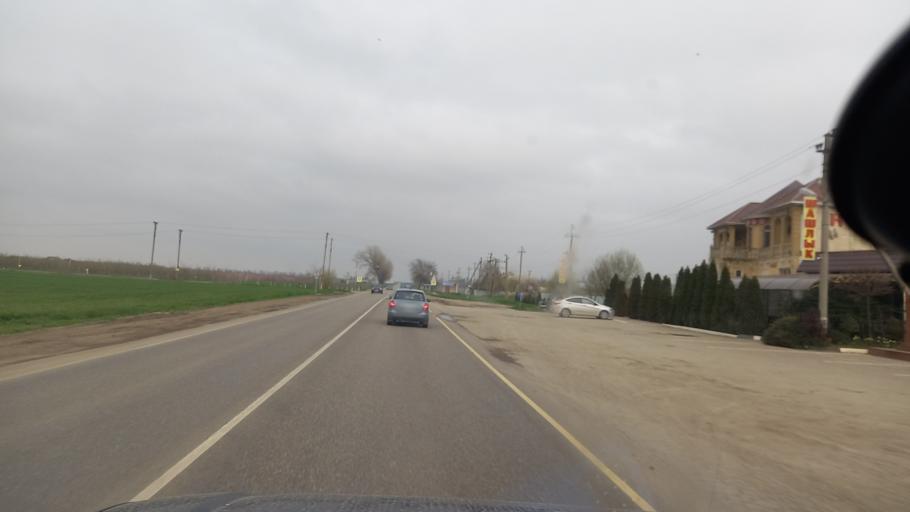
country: RU
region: Krasnodarskiy
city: Slavyansk-na-Kubani
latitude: 45.2430
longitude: 38.0366
